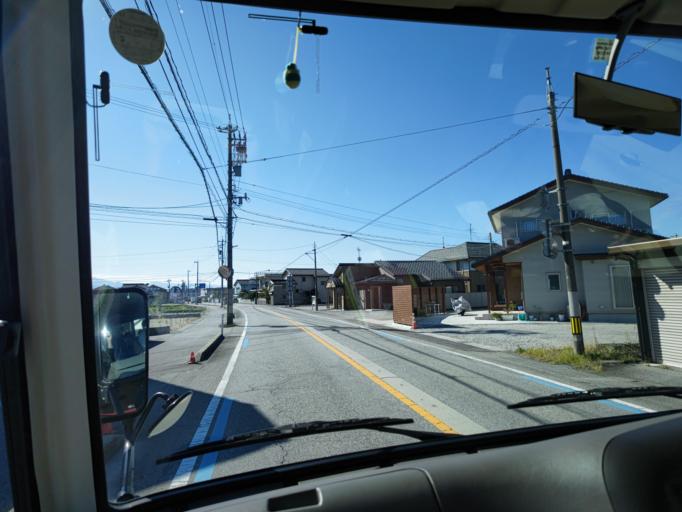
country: JP
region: Toyama
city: Nyuzen
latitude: 36.8968
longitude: 137.4195
